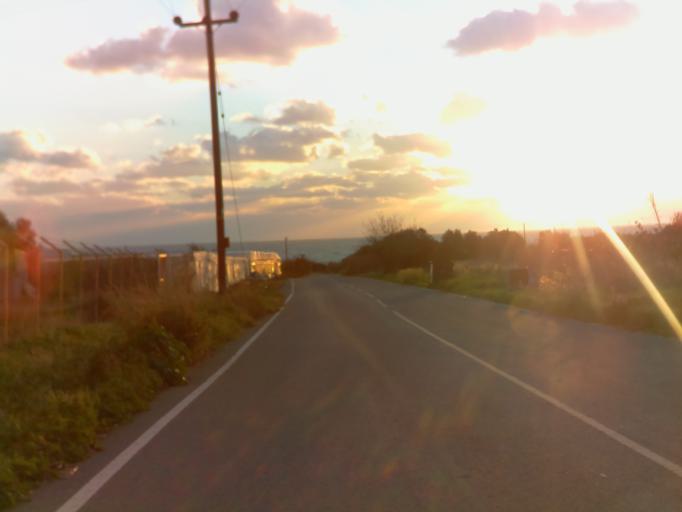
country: CY
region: Pafos
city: Kissonerga
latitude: 34.8466
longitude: 32.3891
